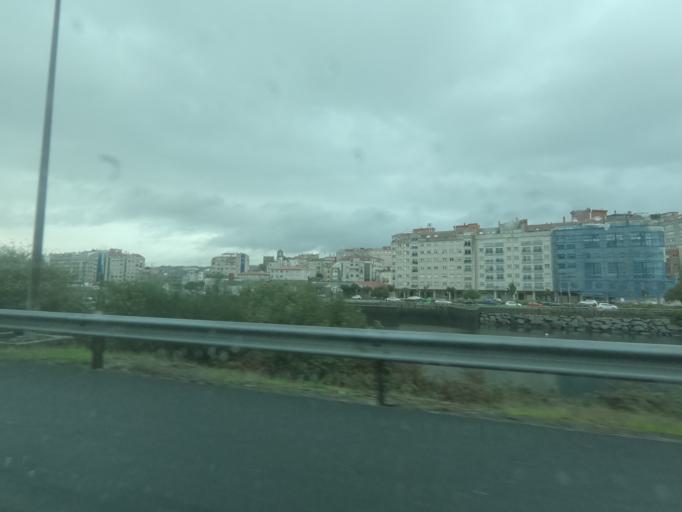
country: ES
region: Galicia
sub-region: Provincia de Pontevedra
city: Pontevedra
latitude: 42.4341
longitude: -8.6525
